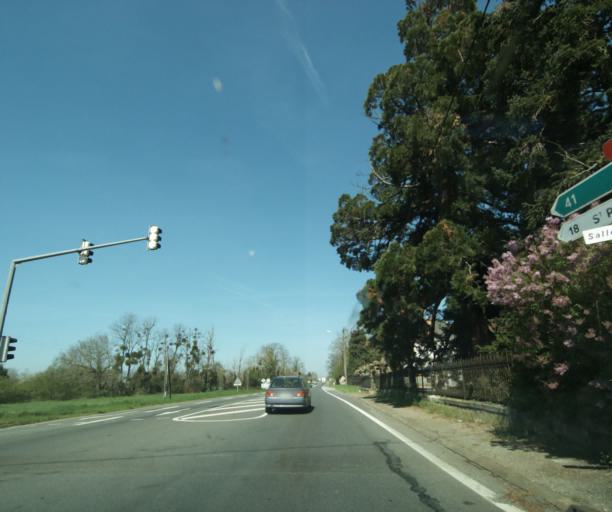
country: FR
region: Auvergne
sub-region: Departement de l'Allier
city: Trevol
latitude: 46.6622
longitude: 3.2456
